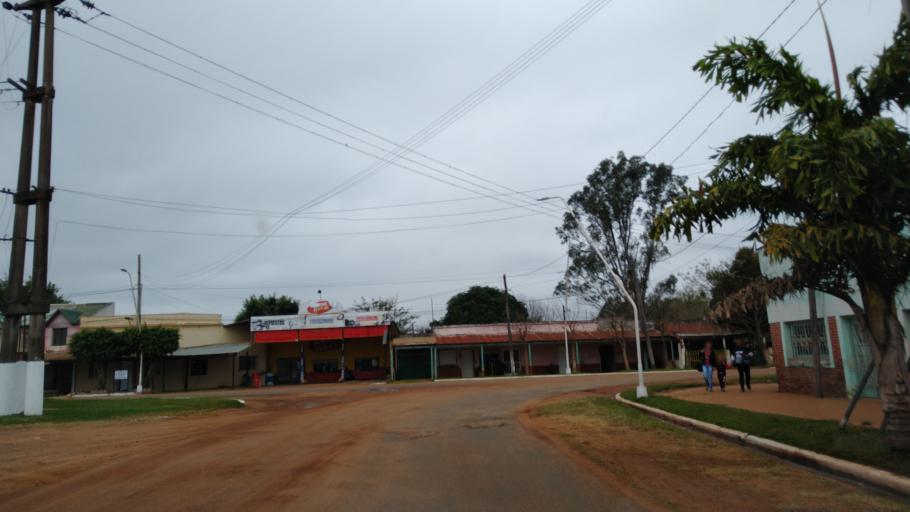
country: AR
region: Corrientes
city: Alvear
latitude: -29.0874
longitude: -56.5473
